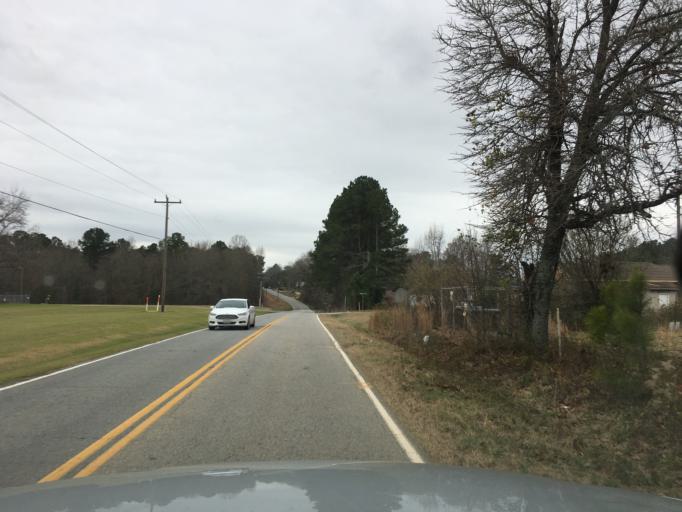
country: US
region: South Carolina
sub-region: Greenwood County
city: Greenwood
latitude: 34.2257
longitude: -82.1068
